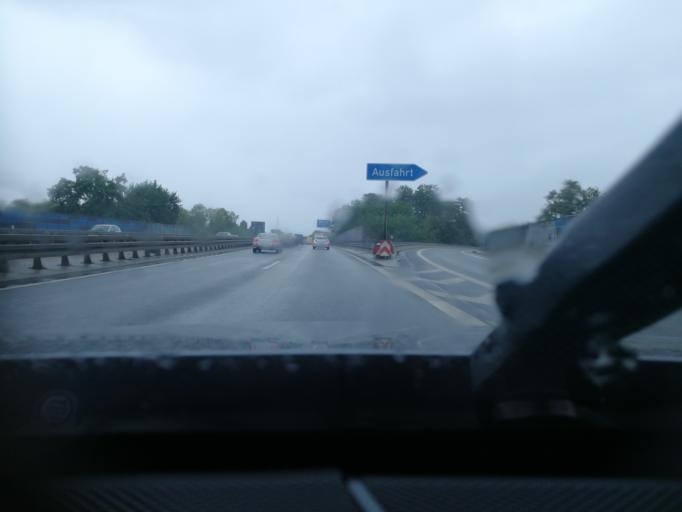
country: DE
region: North Rhine-Westphalia
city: Meiderich
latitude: 51.4674
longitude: 6.7674
